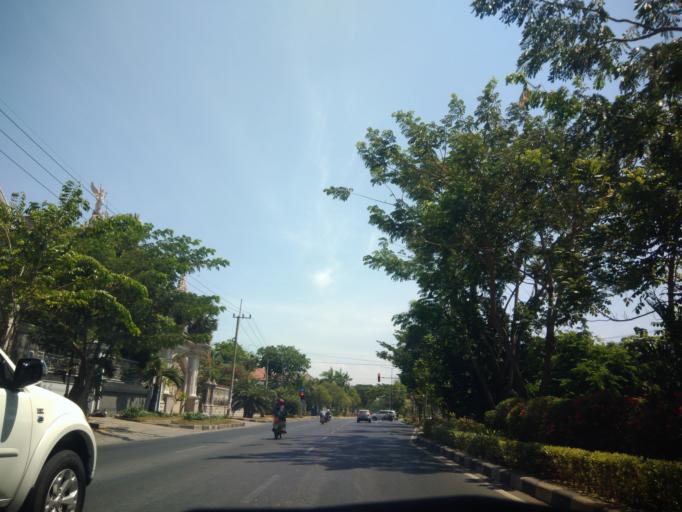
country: ID
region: East Java
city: Mulyorejo
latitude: -7.2710
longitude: 112.7820
